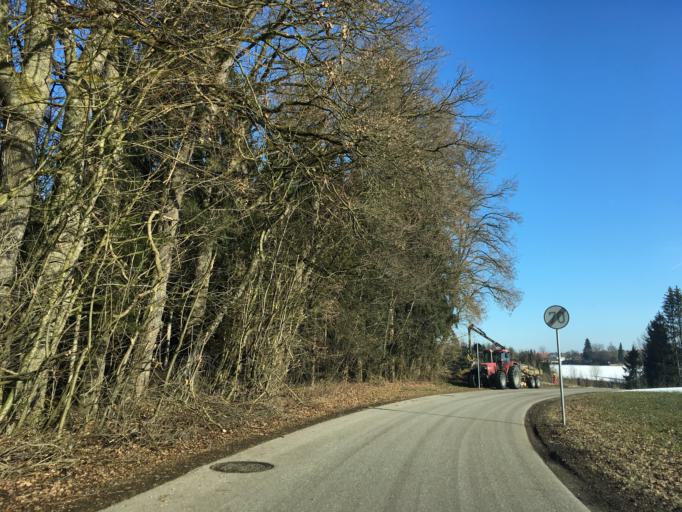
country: DE
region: Bavaria
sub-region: Upper Bavaria
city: Vogtareuth
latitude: 47.9317
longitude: 12.1665
